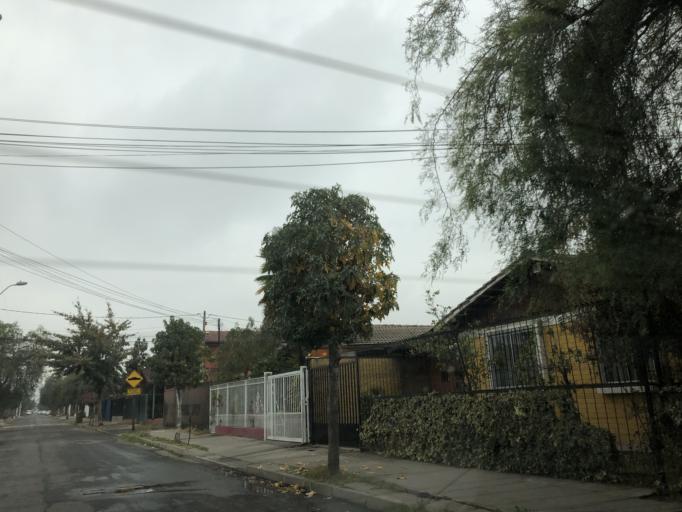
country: CL
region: Santiago Metropolitan
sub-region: Provincia de Cordillera
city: Puente Alto
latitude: -33.5894
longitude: -70.5929
